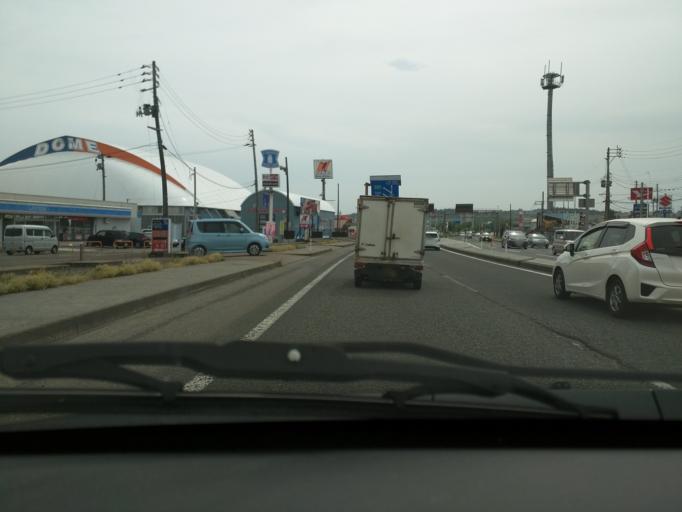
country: JP
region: Niigata
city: Nagaoka
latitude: 37.4473
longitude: 138.7981
